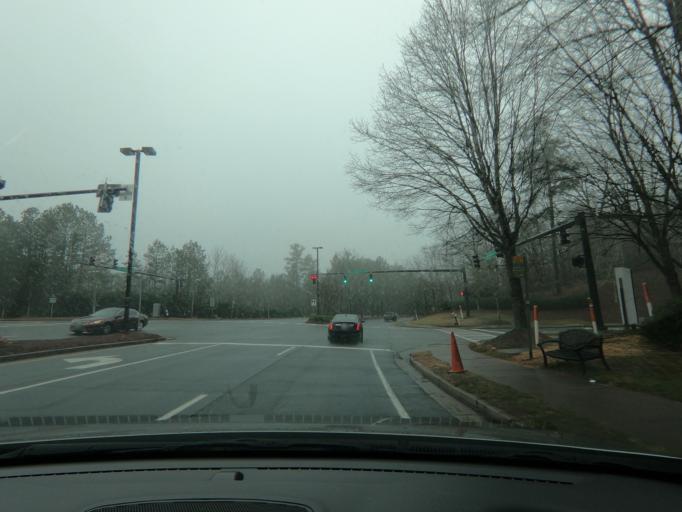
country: US
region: Georgia
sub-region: Fulton County
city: Alpharetta
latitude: 34.0716
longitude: -84.2567
